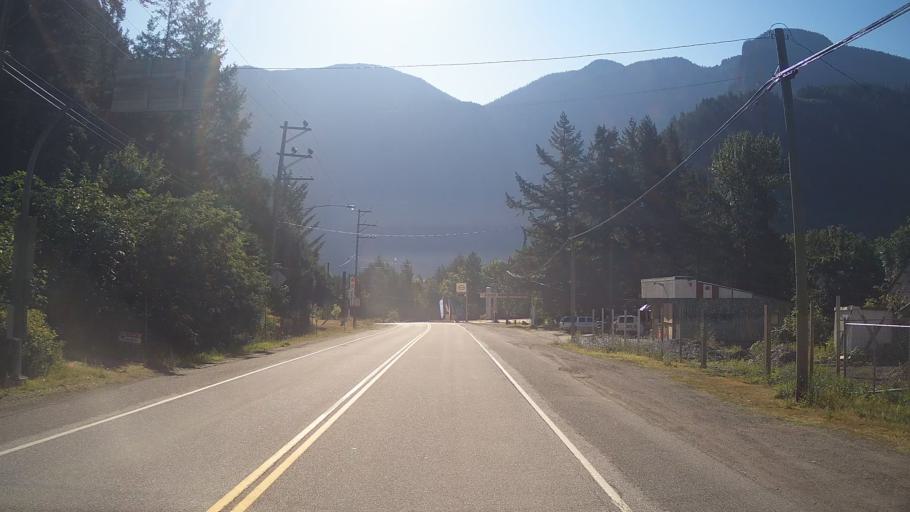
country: CA
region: British Columbia
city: Hope
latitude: 49.5630
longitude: -121.4304
